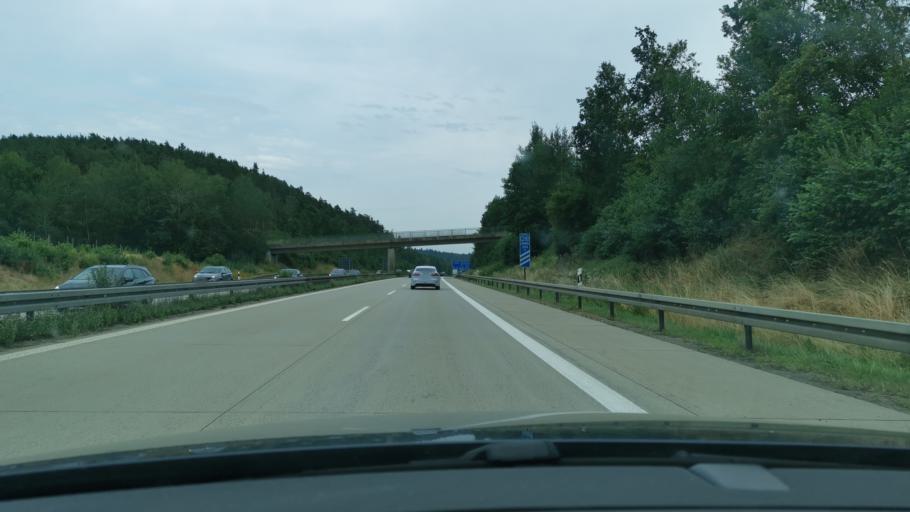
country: DE
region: Bavaria
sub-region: Upper Palatinate
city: Wernberg-Koblitz
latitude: 49.5256
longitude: 12.1531
